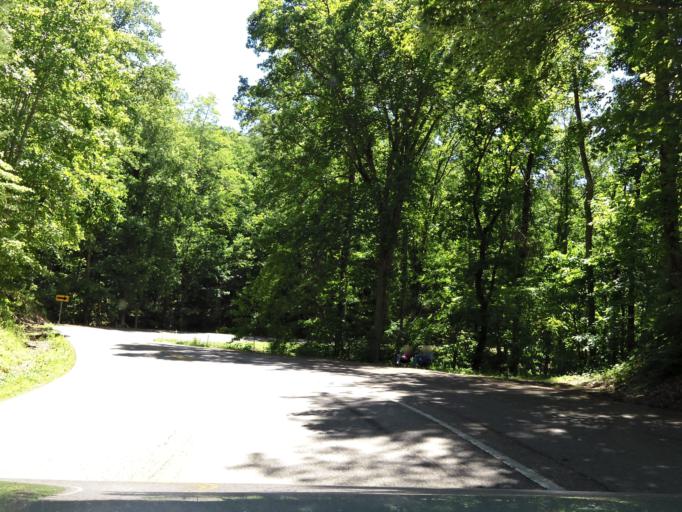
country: US
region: North Carolina
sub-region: Graham County
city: Robbinsville
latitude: 35.5058
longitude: -83.9491
